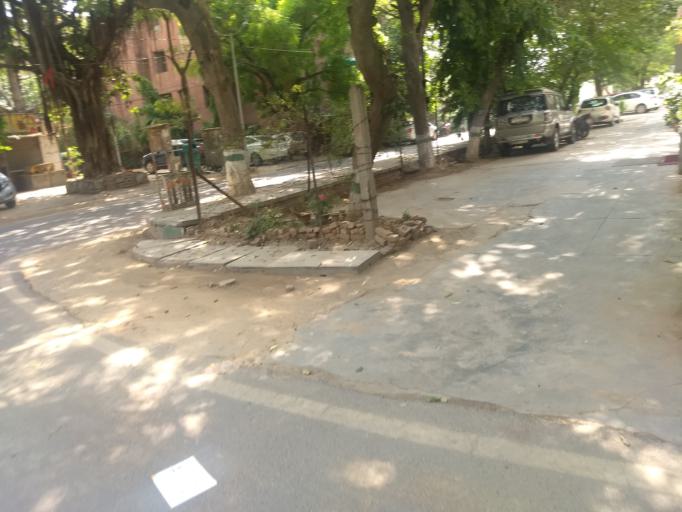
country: IN
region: NCT
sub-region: New Delhi
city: New Delhi
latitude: 28.5589
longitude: 77.2237
